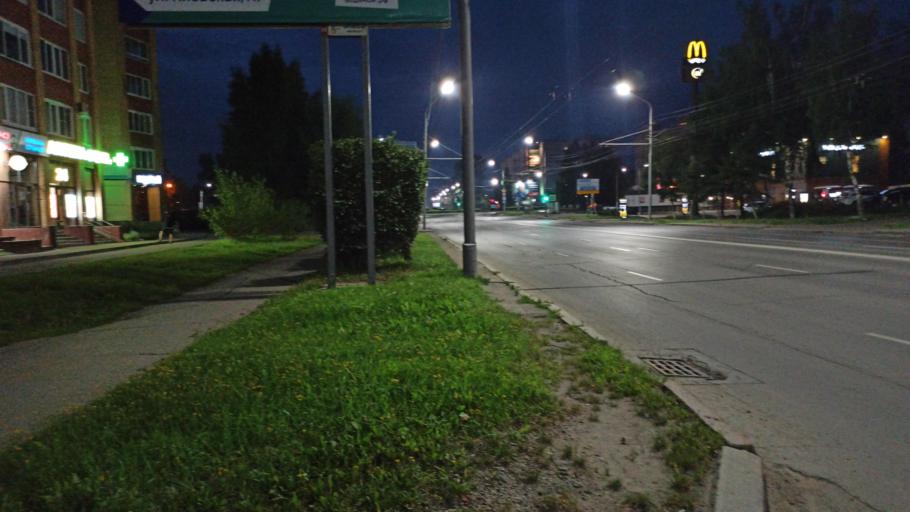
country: RU
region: Tomsk
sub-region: Tomskiy Rayon
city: Tomsk
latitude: 56.4570
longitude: 84.9736
